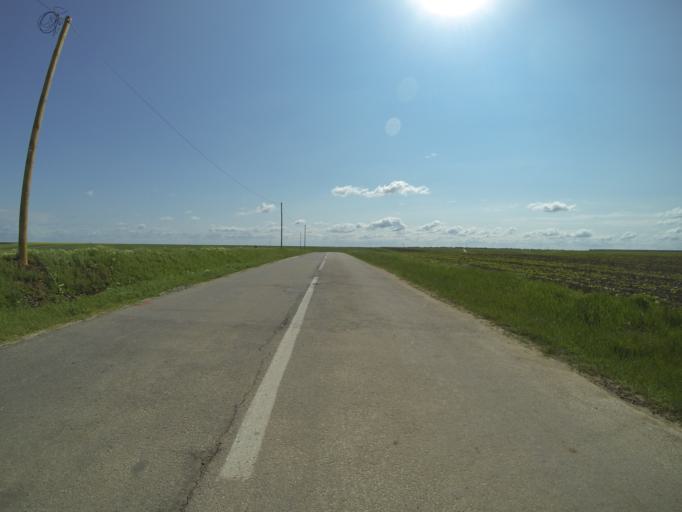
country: RO
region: Dolj
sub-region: Comuna Orodelu
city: Orodelu
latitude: 44.2434
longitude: 23.2207
